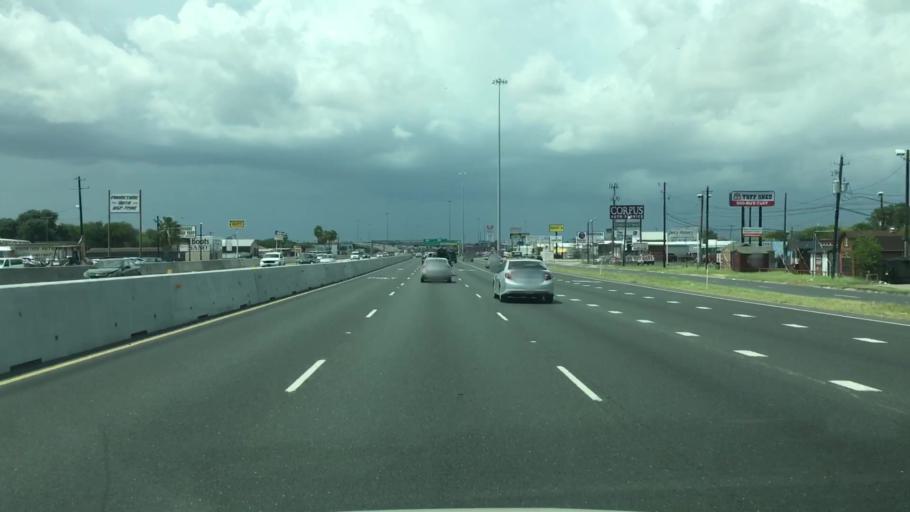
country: US
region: Texas
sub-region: Nueces County
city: Corpus Christi
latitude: 27.7320
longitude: -97.4189
